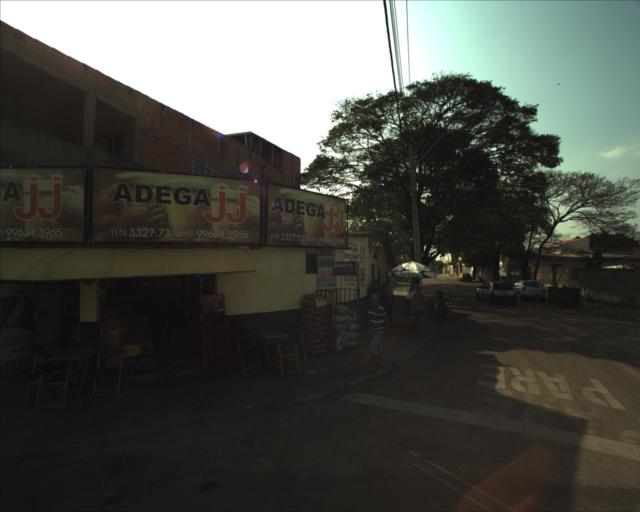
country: BR
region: Sao Paulo
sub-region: Sorocaba
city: Sorocaba
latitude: -23.4362
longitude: -47.4688
